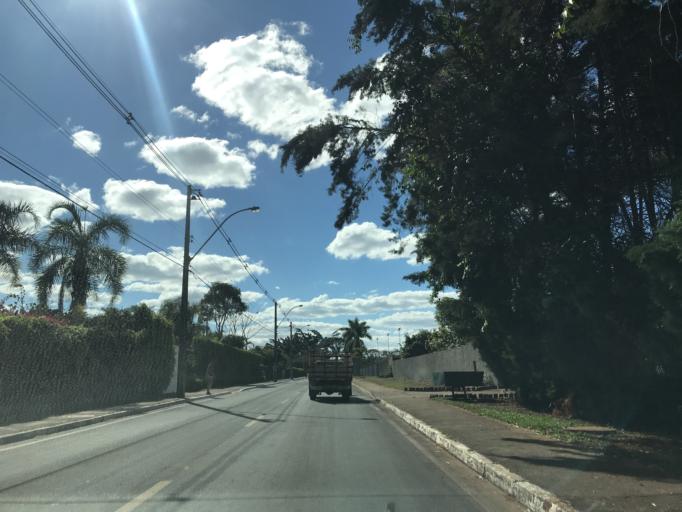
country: BR
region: Federal District
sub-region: Brasilia
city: Brasilia
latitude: -15.7564
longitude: -47.8425
